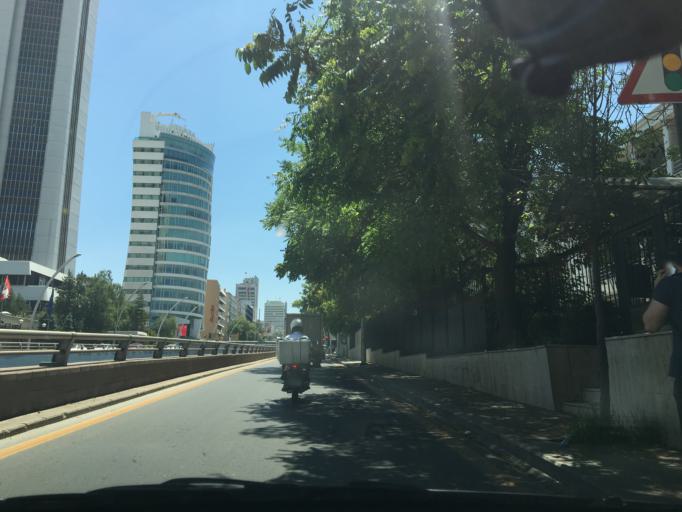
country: TR
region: Ankara
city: Ankara
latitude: 39.9099
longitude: 32.8558
